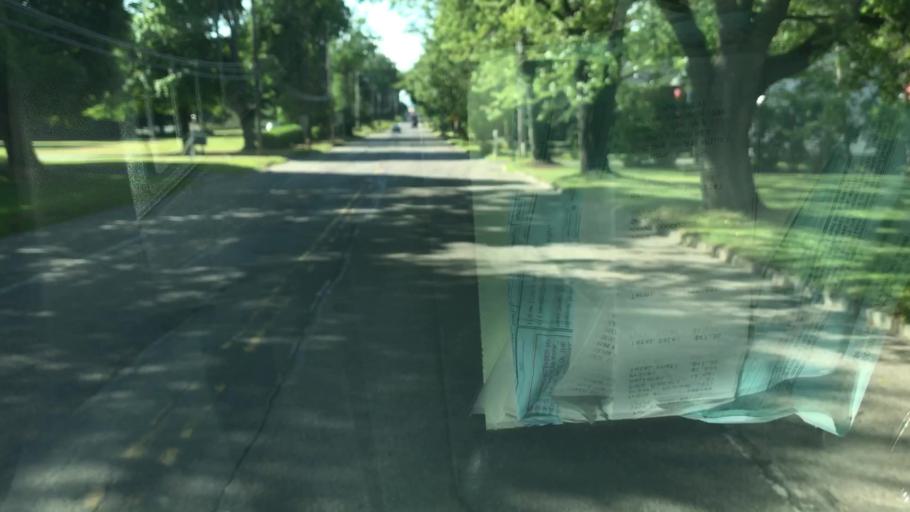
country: US
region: New York
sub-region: Onondaga County
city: Skaneateles
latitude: 42.9390
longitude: -76.4116
